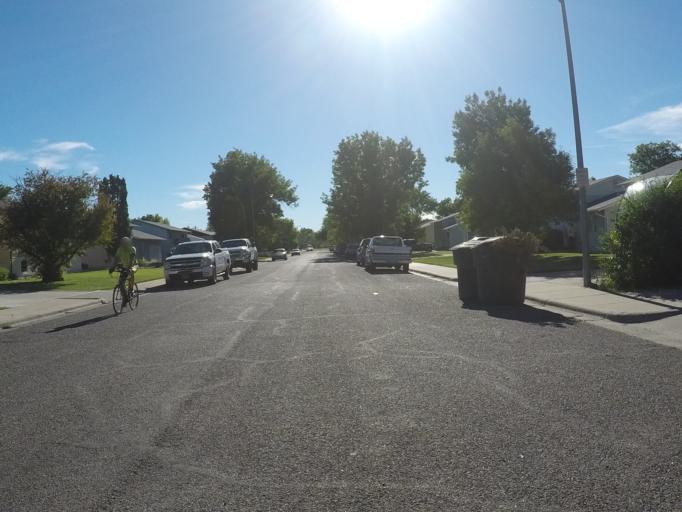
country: US
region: Montana
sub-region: Yellowstone County
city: Billings
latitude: 45.7737
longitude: -108.5822
